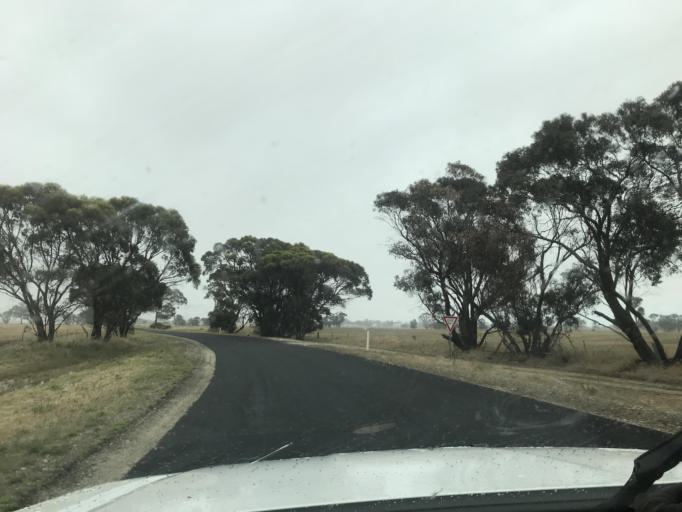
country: AU
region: South Australia
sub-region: Tatiara
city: Bordertown
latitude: -36.3214
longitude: 141.2042
